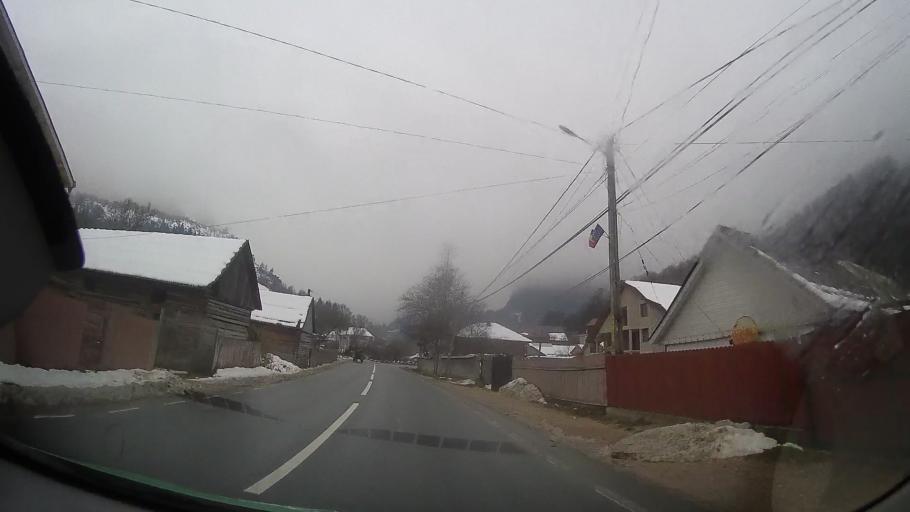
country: RO
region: Neamt
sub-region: Comuna Bicaz Chei
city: Bicaz Chei
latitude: 46.8240
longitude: 25.8632
